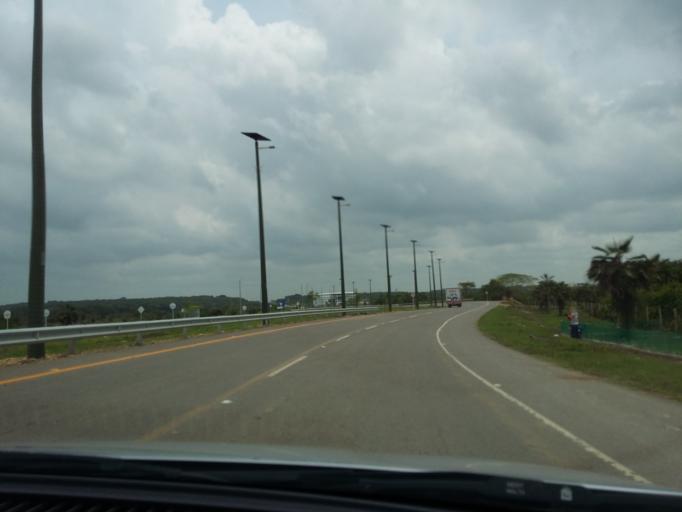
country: CO
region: Bolivar
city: Cartagena
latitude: 10.4995
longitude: -75.4765
